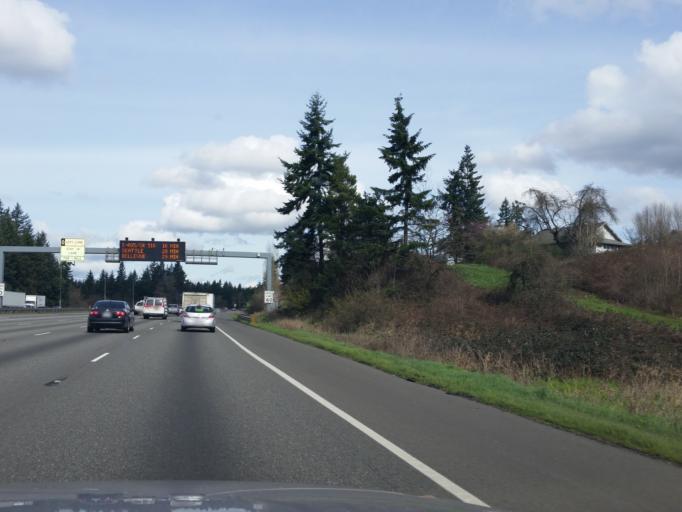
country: US
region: Washington
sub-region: Pierce County
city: Fife Heights
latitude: 47.2550
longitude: -122.3311
